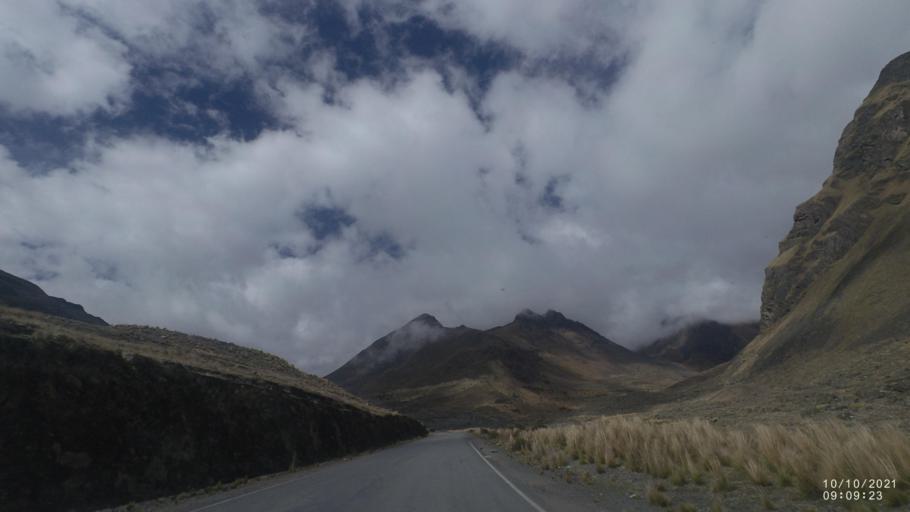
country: BO
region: La Paz
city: Quime
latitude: -17.0224
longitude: -67.2817
